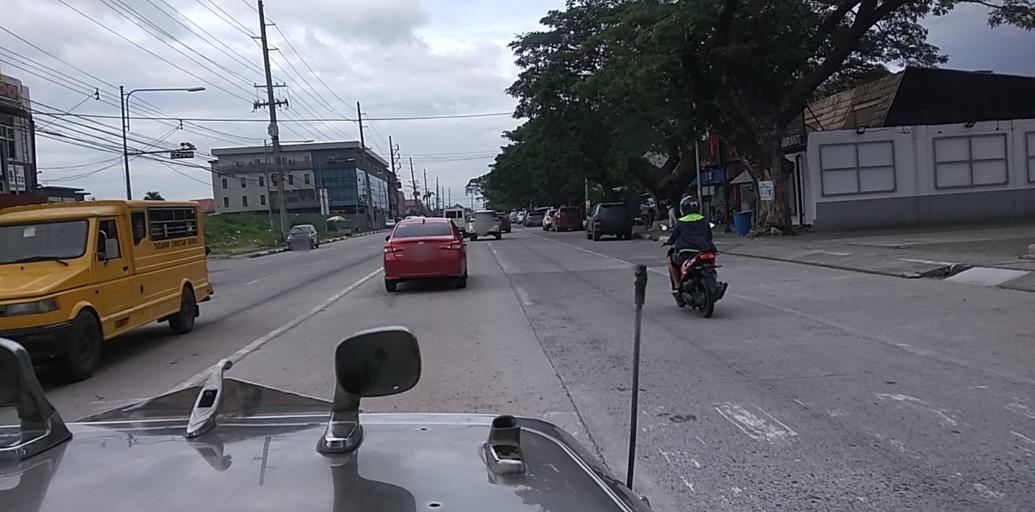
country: PH
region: Central Luzon
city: Santol
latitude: 15.1478
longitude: 120.5594
